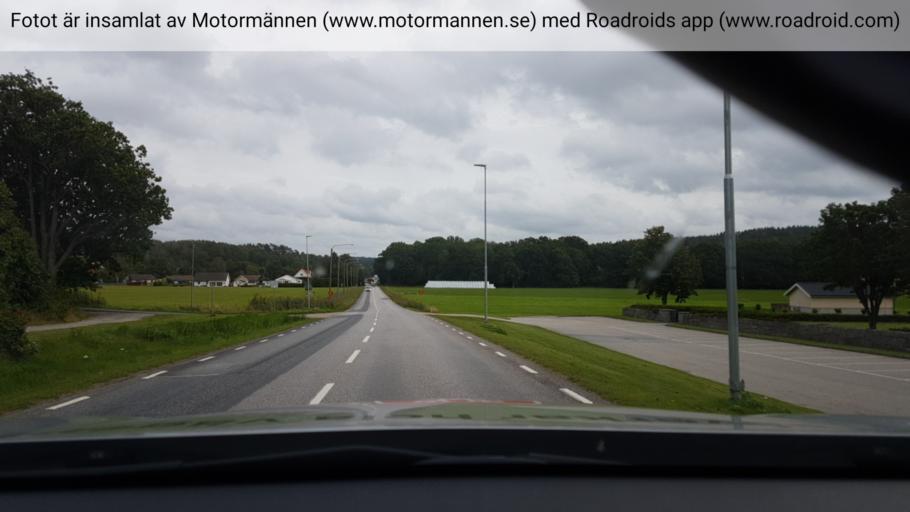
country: SE
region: Vaestra Goetaland
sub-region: Sotenas Kommun
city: Hunnebostrand
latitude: 58.5675
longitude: 11.3707
